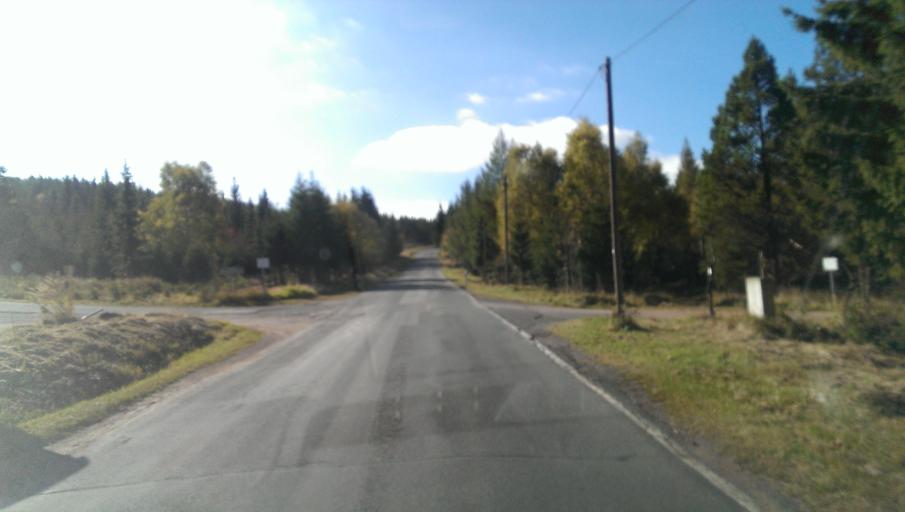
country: DE
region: Saxony
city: Altenberg
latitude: 50.7558
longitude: 13.7354
